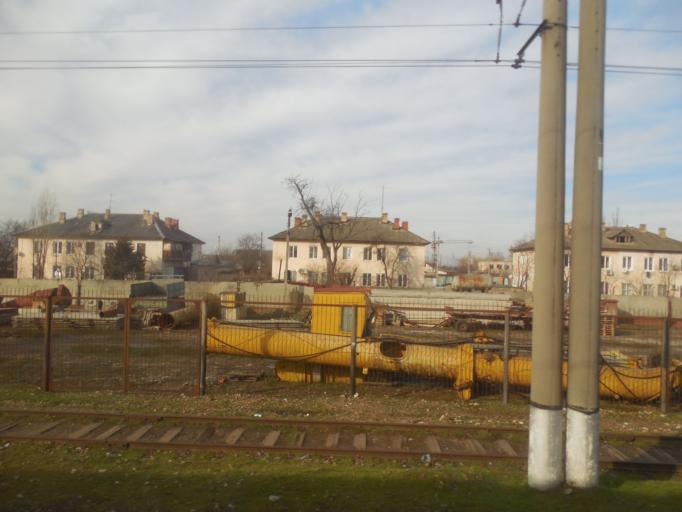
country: RU
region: Adygeya
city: Enem
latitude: 44.9255
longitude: 38.9037
